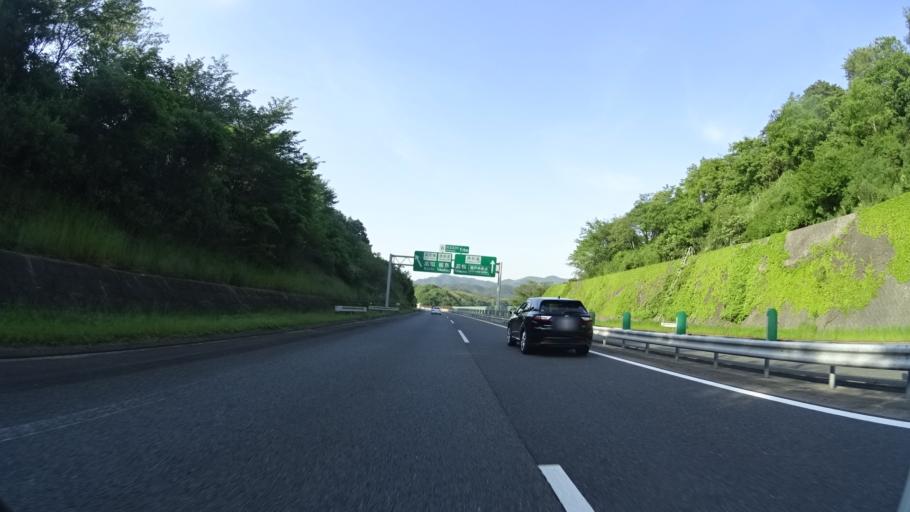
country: JP
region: Ehime
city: Kawanoecho
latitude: 33.9880
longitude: 133.5915
